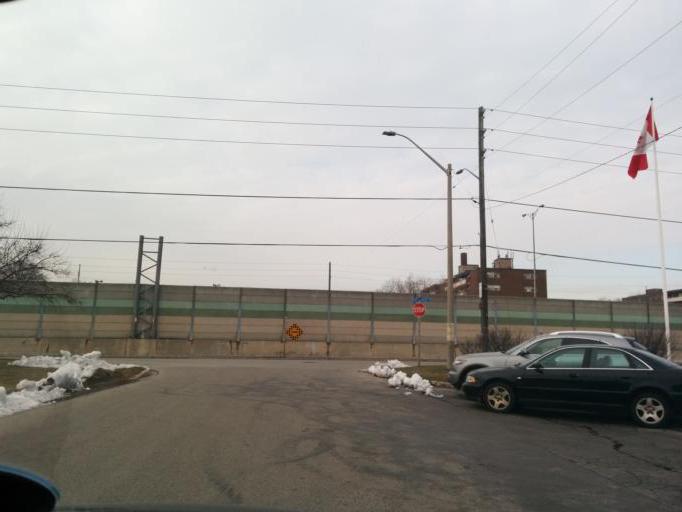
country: CA
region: Ontario
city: Mississauga
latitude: 43.5787
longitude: -79.5874
